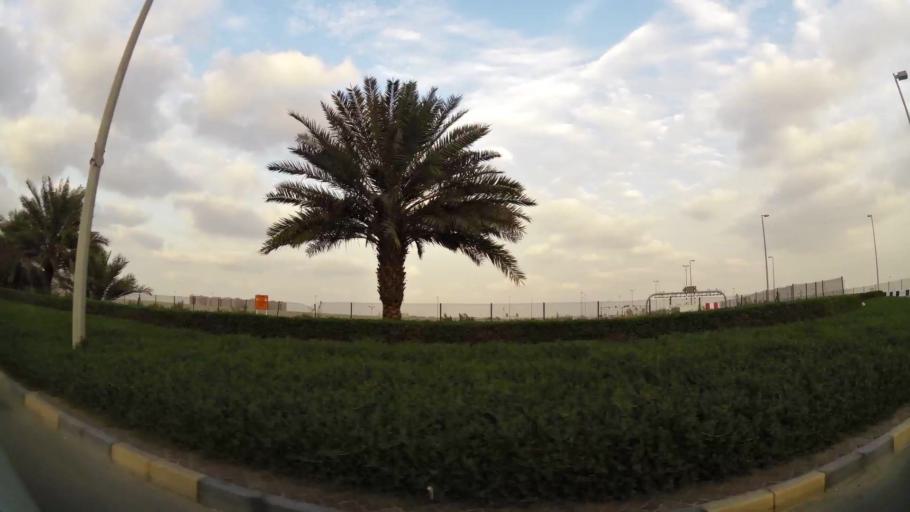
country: AE
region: Abu Dhabi
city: Abu Dhabi
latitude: 24.3606
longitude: 54.5257
